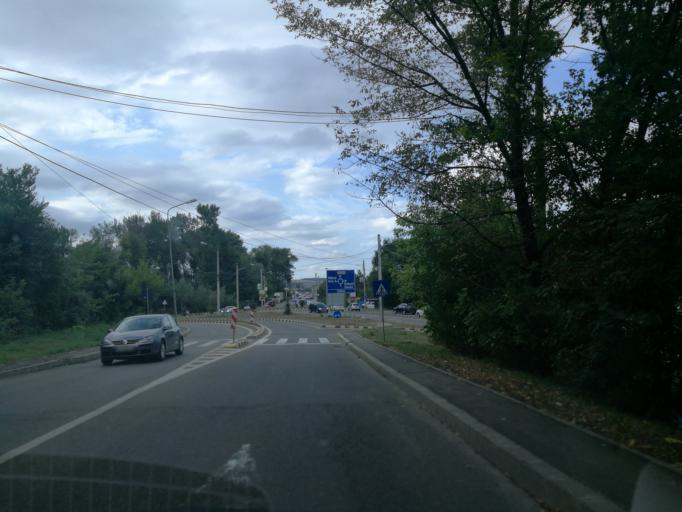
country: RO
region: Suceava
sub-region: Comuna Scheia
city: Scheia
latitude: 47.6631
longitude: 26.2478
